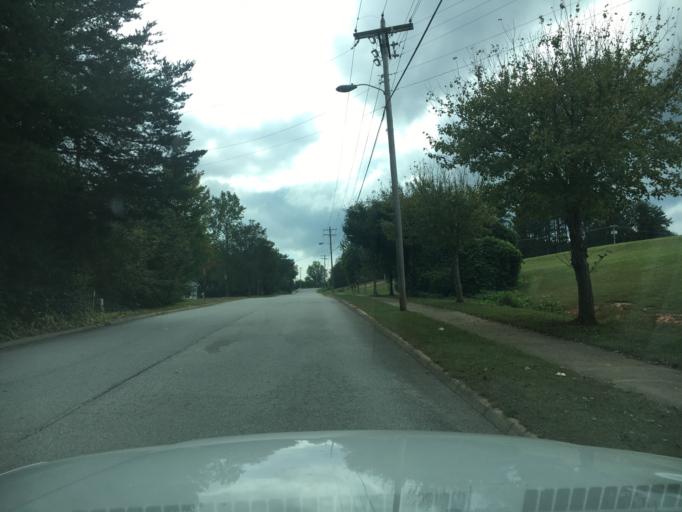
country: US
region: South Carolina
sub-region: Greenville County
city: Greer
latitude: 34.9541
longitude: -82.2335
